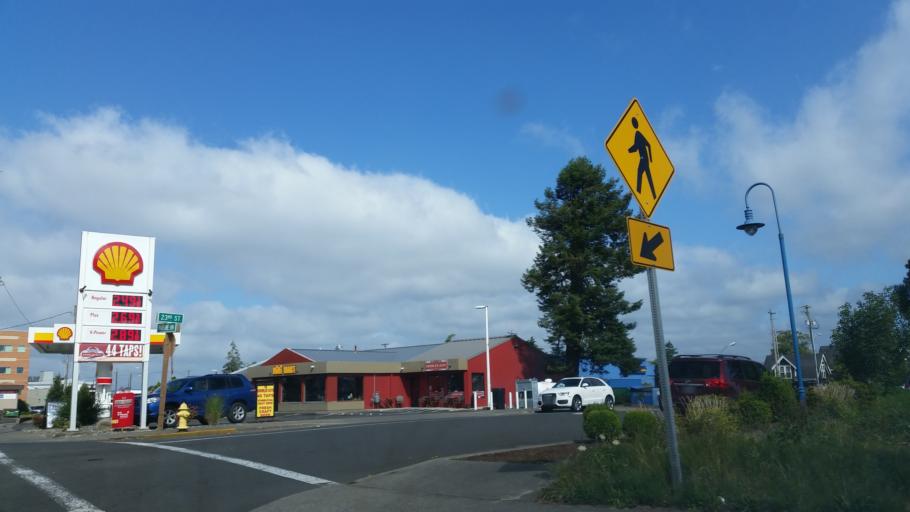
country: US
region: Oregon
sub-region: Clatsop County
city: Astoria
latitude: 46.1887
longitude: -123.8156
